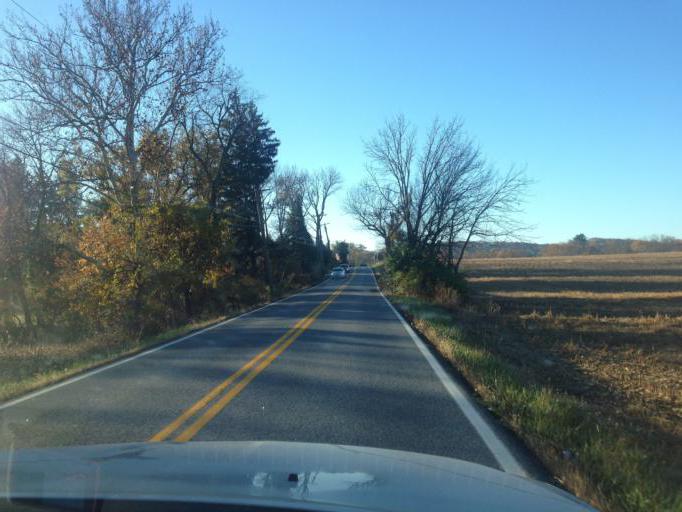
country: US
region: Maryland
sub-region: Baltimore County
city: Mays Chapel
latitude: 39.4243
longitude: -76.6908
